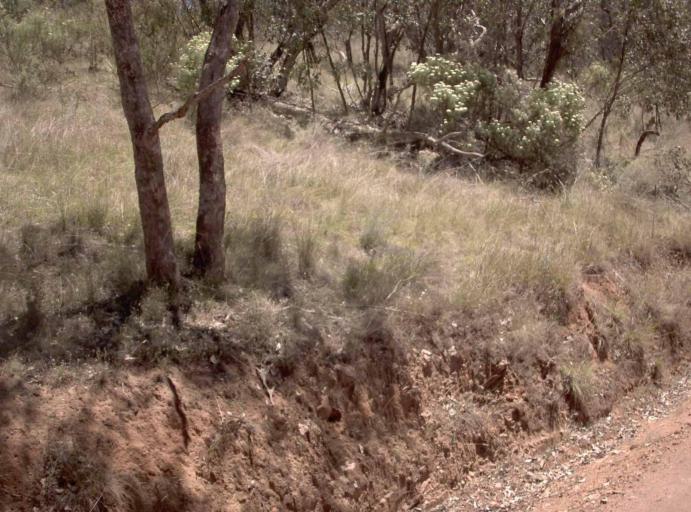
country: AU
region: New South Wales
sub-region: Snowy River
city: Jindabyne
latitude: -36.9393
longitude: 148.3441
